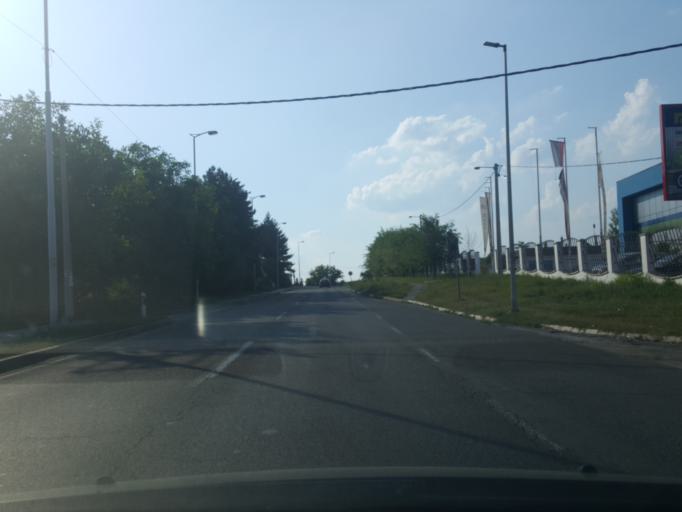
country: RS
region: Central Serbia
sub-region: Belgrade
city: Mladenovac
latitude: 44.4516
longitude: 20.6827
